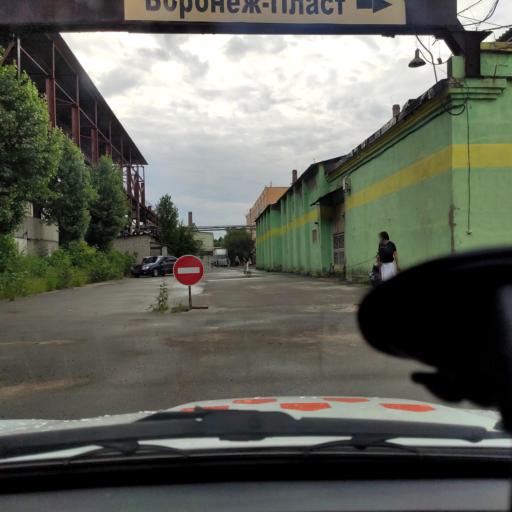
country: RU
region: Voronezj
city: Voronezh
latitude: 51.6625
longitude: 39.1773
